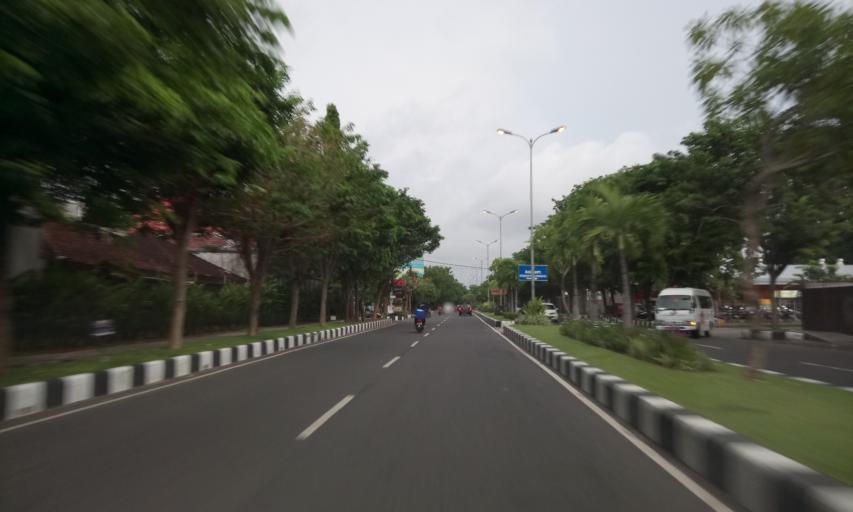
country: ID
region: Bali
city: Kelanabian
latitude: -8.7439
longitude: 115.1719
